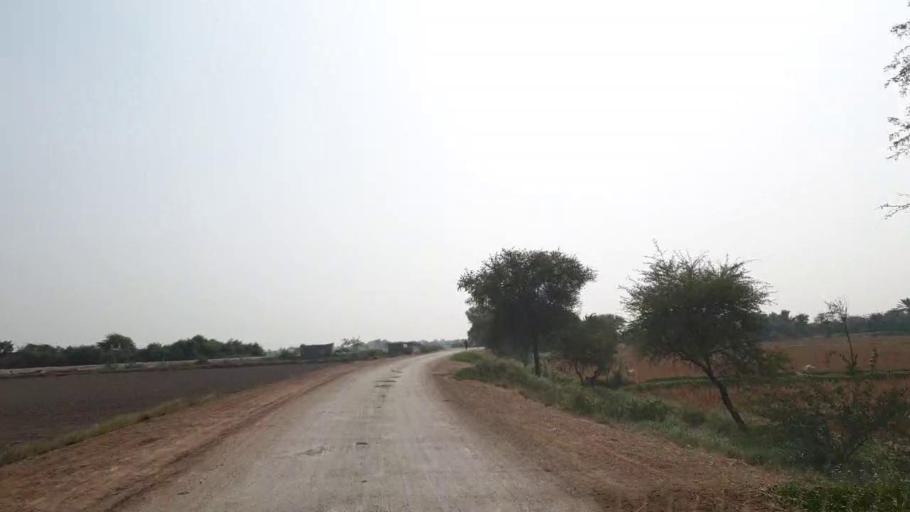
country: PK
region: Sindh
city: Matli
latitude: 24.9759
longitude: 68.5838
